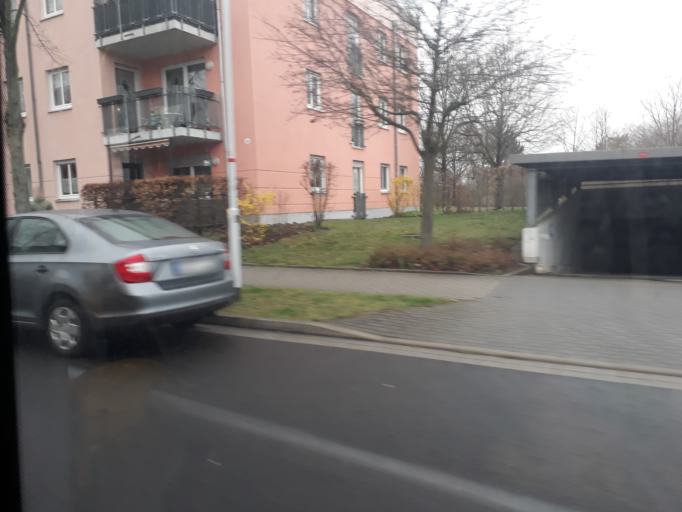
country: DE
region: Saxony
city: Kreischa
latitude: 50.9921
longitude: 13.7889
